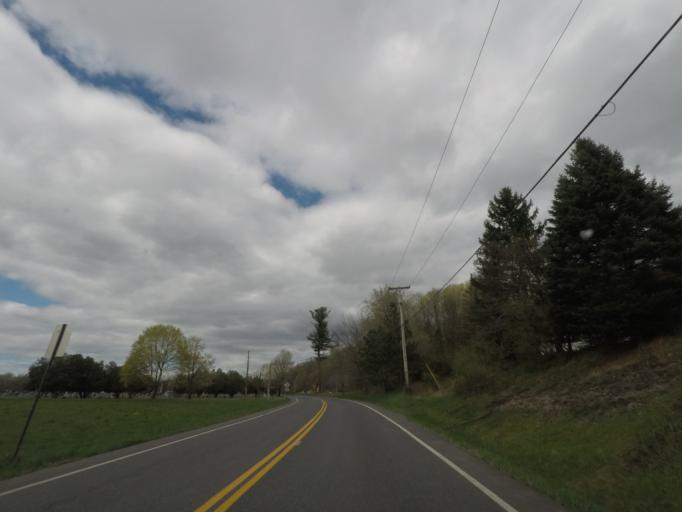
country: US
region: New York
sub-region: Columbia County
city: Chatham
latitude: 42.3114
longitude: -73.6276
